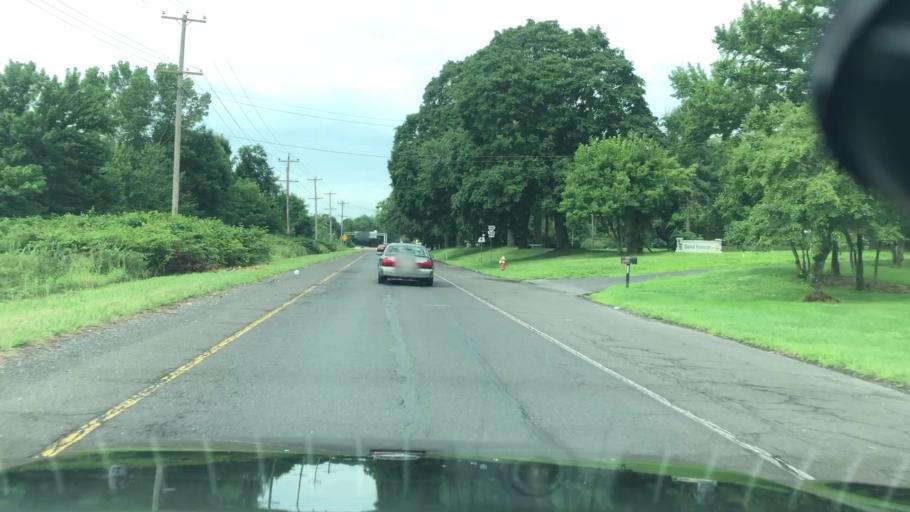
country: US
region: Pennsylvania
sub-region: Bucks County
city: Morrisville
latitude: 40.1999
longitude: -74.7901
